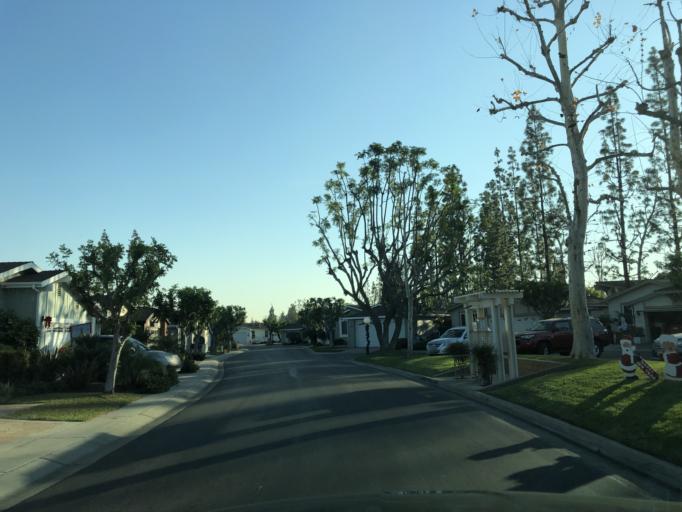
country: US
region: California
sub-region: Orange County
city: Orange
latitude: 33.7725
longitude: -117.8455
